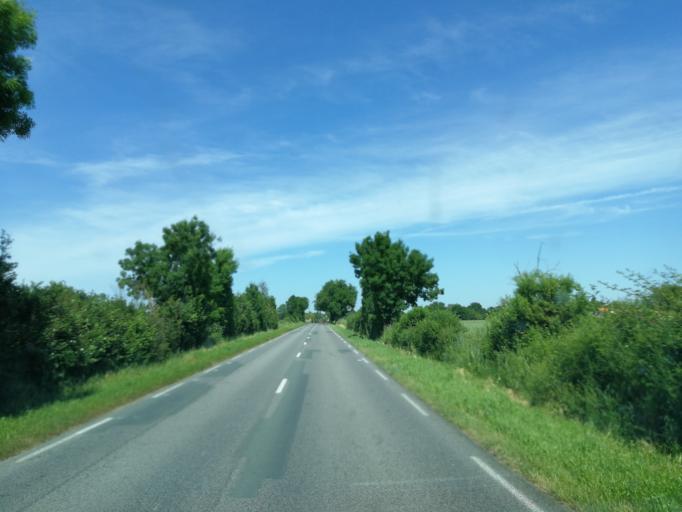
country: FR
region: Poitou-Charentes
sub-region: Departement des Deux-Sevres
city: Saint-Varent
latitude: 46.8963
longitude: -0.2948
